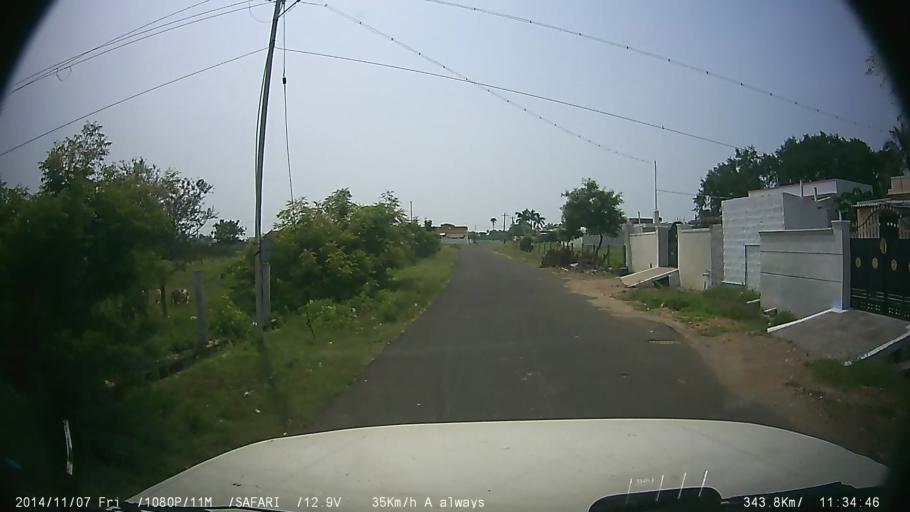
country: IN
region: Tamil Nadu
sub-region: Tiruppur
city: Avinashi
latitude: 11.1583
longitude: 77.2801
